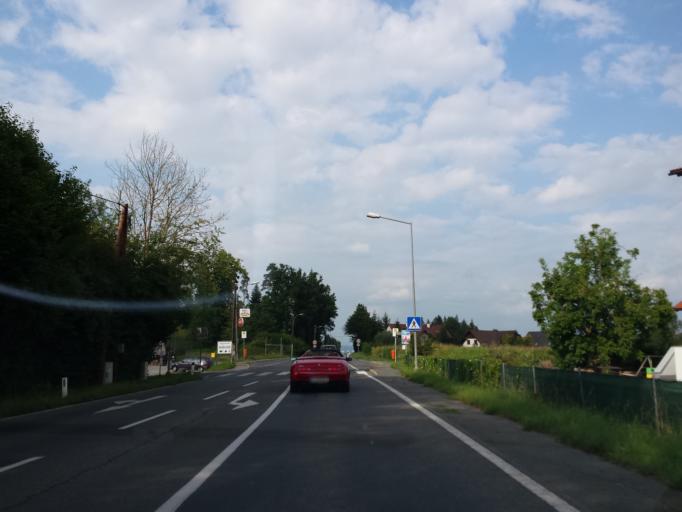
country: AT
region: Styria
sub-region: Politischer Bezirk Graz-Umgebung
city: Pirka
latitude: 46.9952
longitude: 15.3837
